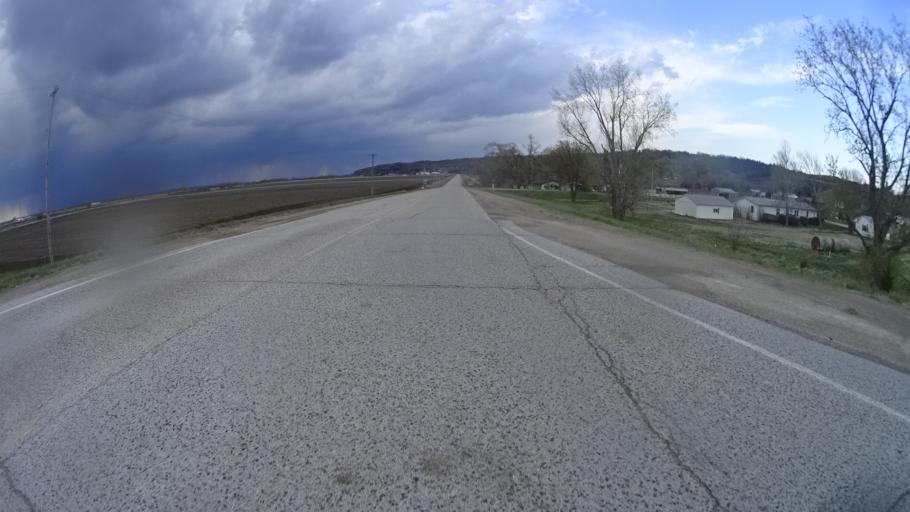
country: US
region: Iowa
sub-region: Mills County
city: Glenwood
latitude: 41.0467
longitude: -95.8039
